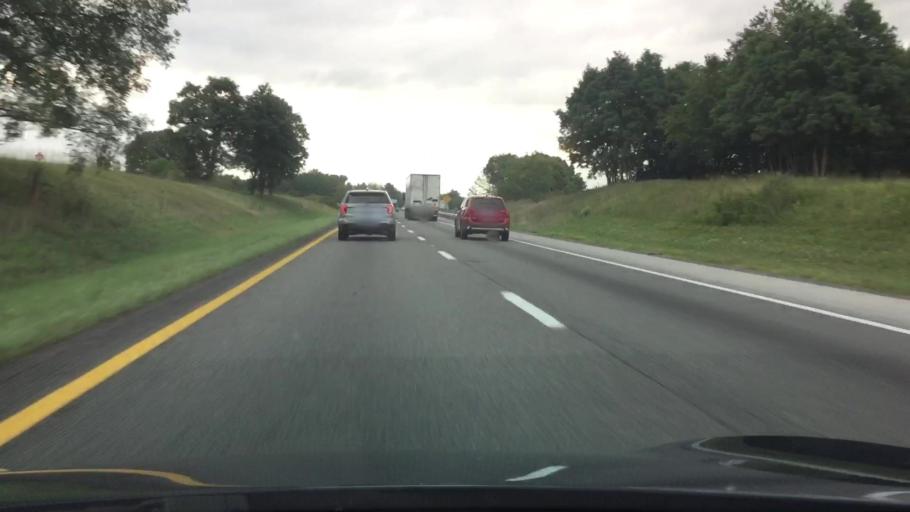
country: US
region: Virginia
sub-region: Pulaski County
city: Dublin
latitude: 37.0767
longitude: -80.6951
